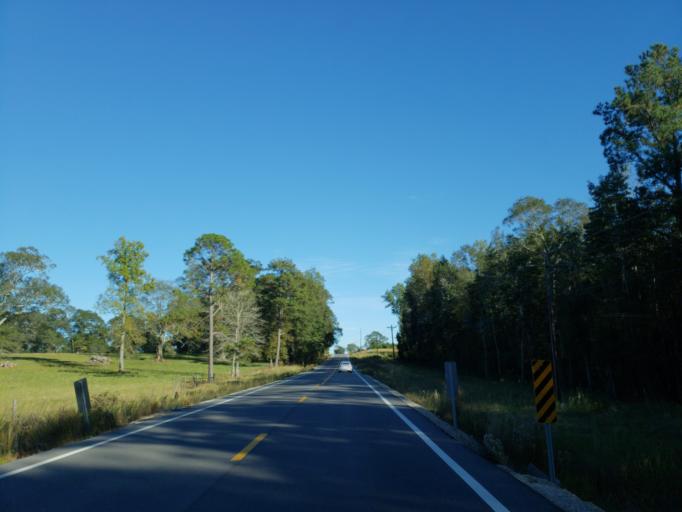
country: US
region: Mississippi
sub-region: Perry County
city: Richton
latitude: 31.3614
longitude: -89.0437
